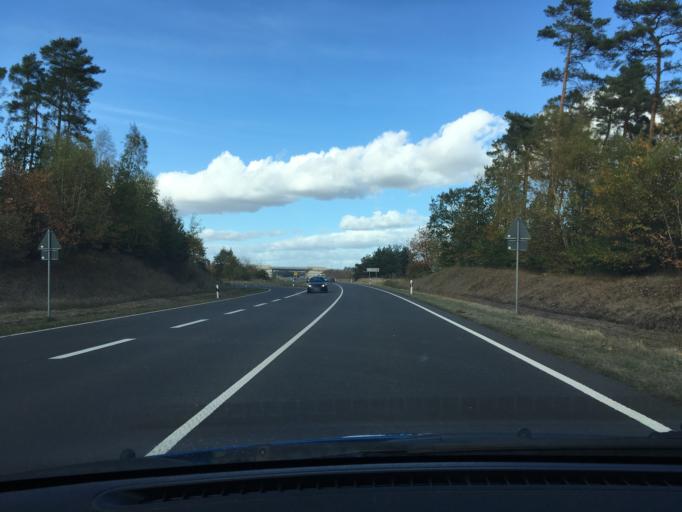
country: DE
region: Brandenburg
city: Perleberg
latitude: 53.0588
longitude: 11.8328
